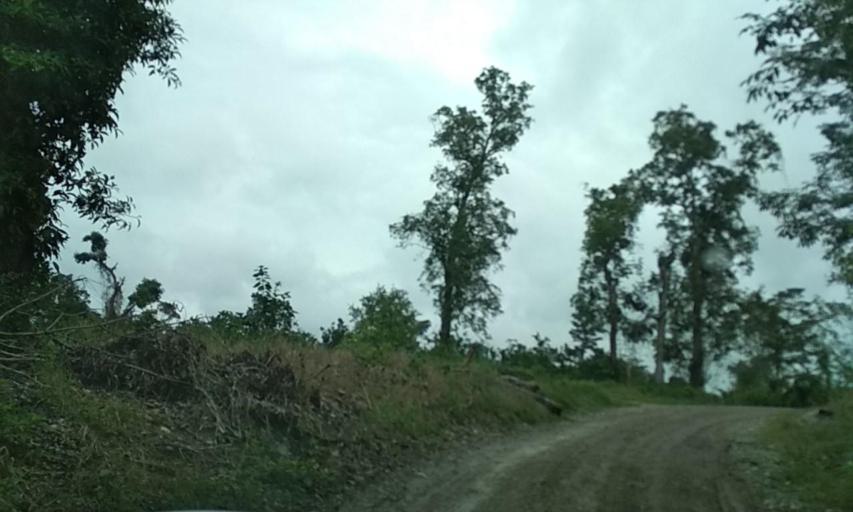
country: MX
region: Puebla
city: Espinal
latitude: 20.3076
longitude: -97.4150
